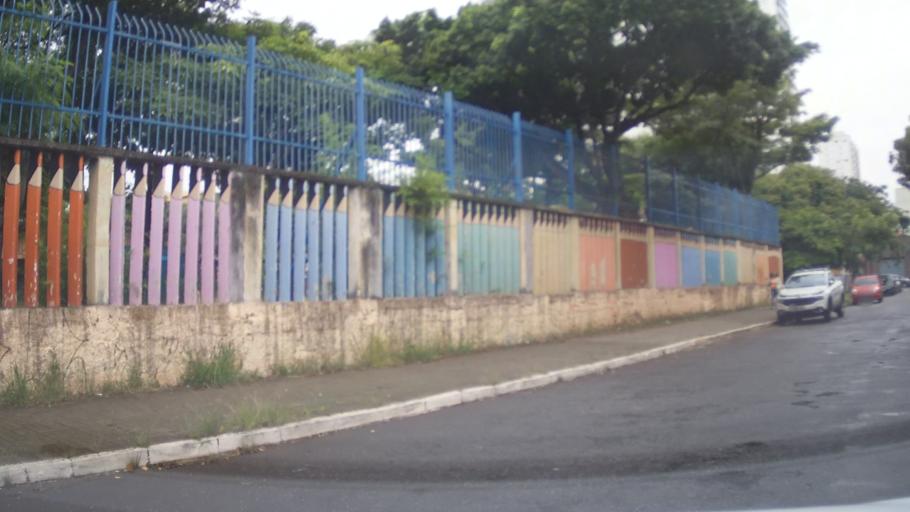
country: BR
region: Sao Paulo
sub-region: Sao Paulo
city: Sao Paulo
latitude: -23.5486
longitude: -46.6175
